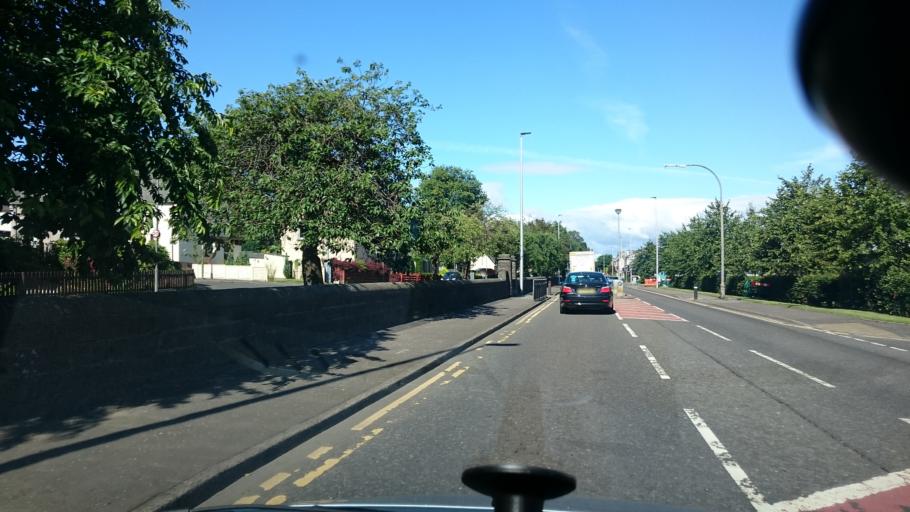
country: GB
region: Scotland
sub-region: Clackmannanshire
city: Alloa
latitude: 56.1160
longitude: -3.7796
